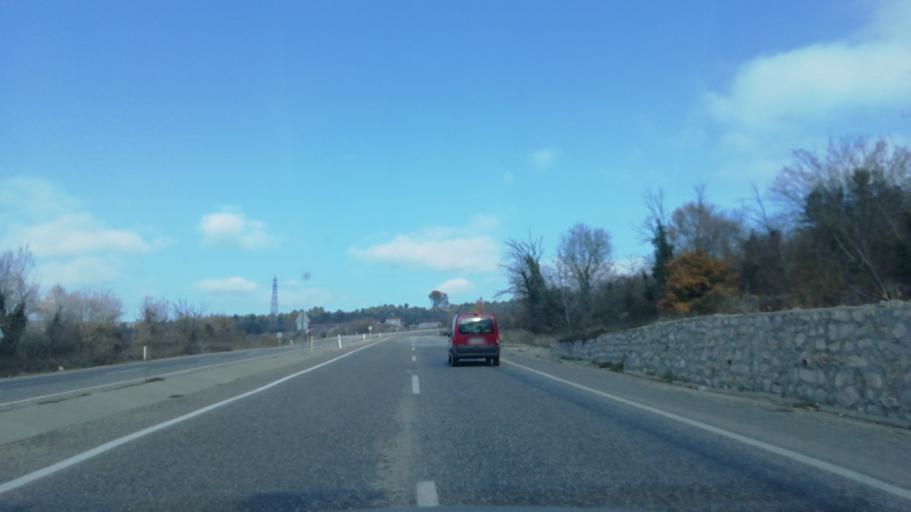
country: TR
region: Karabuk
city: Safranbolu
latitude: 41.2208
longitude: 32.7675
